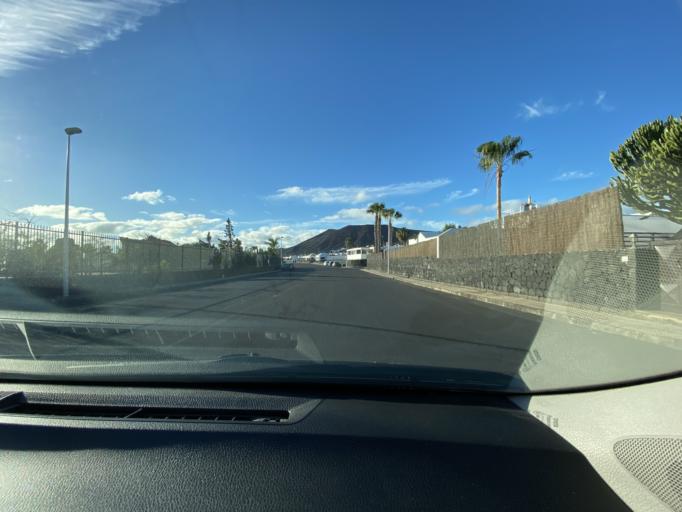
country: ES
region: Canary Islands
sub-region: Provincia de Las Palmas
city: Playa Blanca
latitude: 28.8632
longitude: -13.8432
